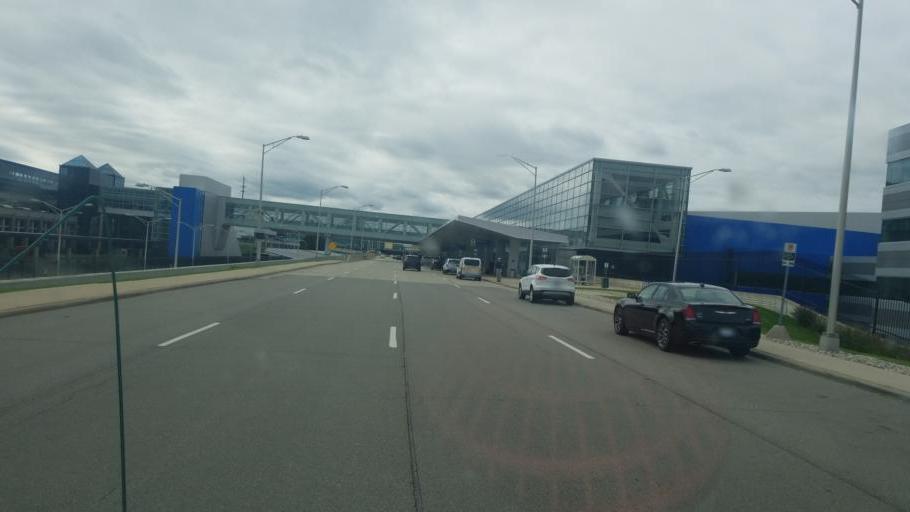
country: US
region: Michigan
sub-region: Wayne County
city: Romulus
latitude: 42.2270
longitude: -83.3466
